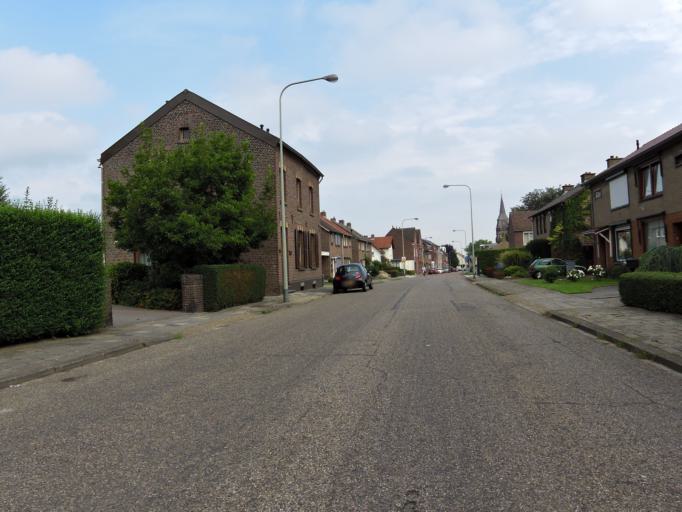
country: NL
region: Limburg
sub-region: Gemeente Kerkrade
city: Kerkrade
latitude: 50.9131
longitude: 6.0527
